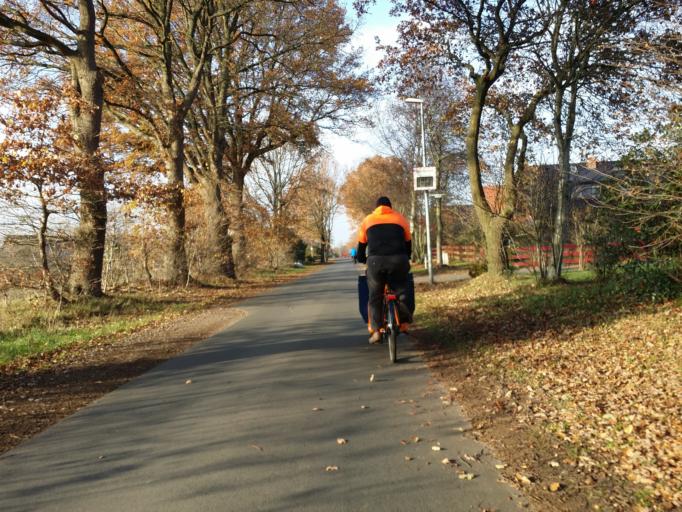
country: DE
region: Lower Saxony
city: Botersen
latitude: 53.1092
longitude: 9.3304
